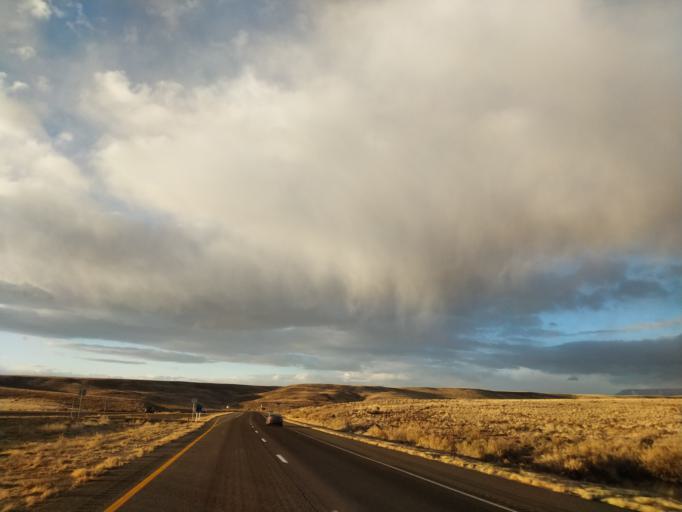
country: US
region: Colorado
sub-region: Delta County
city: Delta
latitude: 38.8072
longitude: -108.2766
